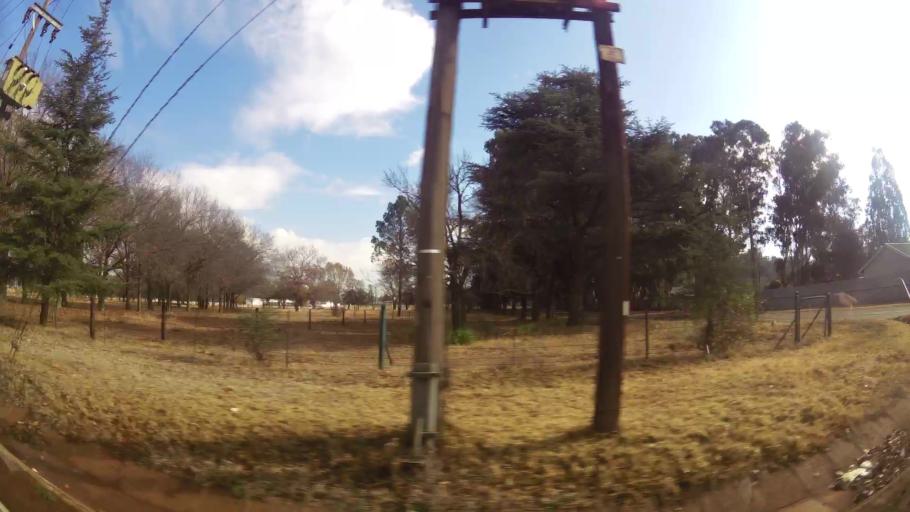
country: ZA
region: Gauteng
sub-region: Sedibeng District Municipality
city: Meyerton
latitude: -26.5518
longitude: 28.0562
